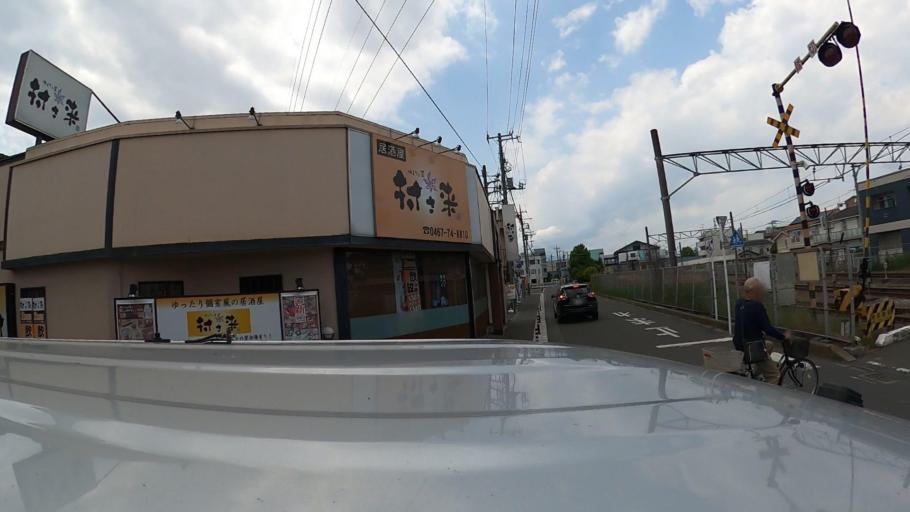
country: JP
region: Kanagawa
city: Chigasaki
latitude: 35.3664
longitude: 139.3888
